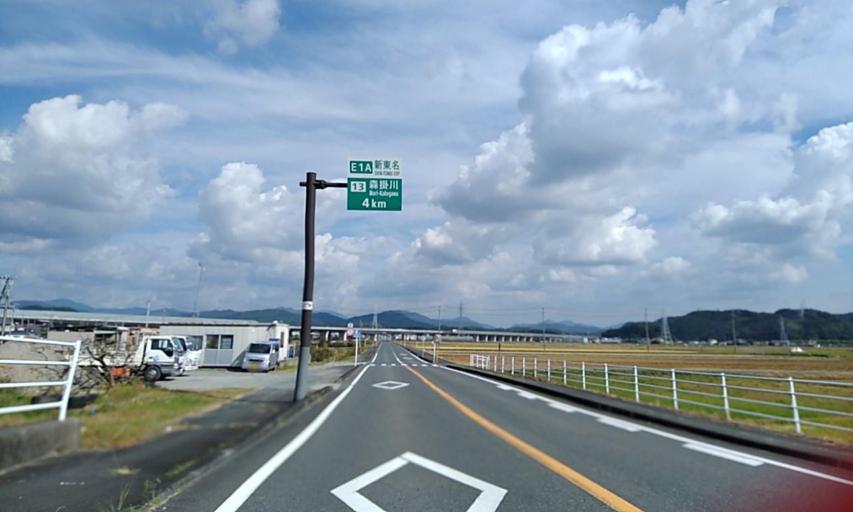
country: JP
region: Shizuoka
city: Mori
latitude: 34.8193
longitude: 137.9089
